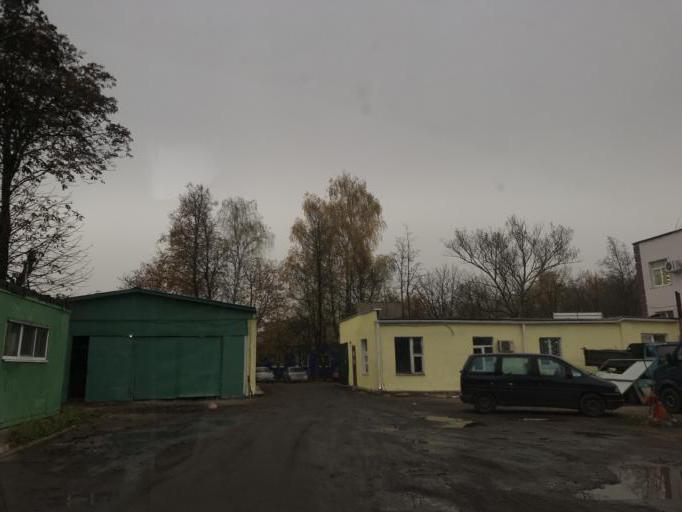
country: BY
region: Mogilev
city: Buynichy
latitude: 53.8936
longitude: 30.2951
